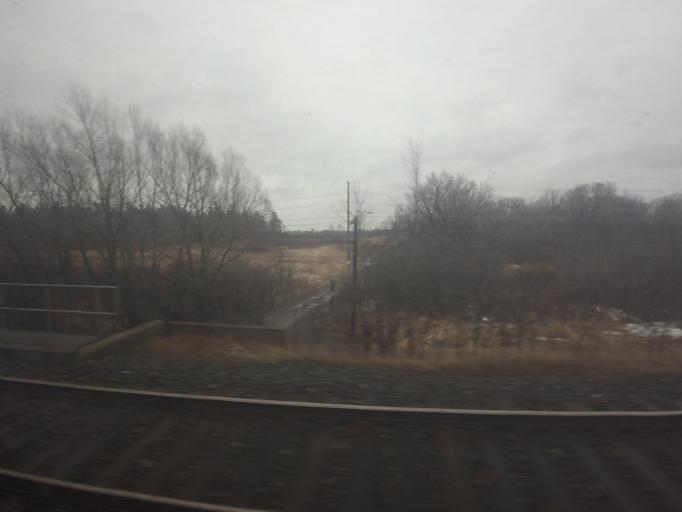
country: CA
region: Ontario
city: Kingston
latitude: 44.2882
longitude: -76.4550
